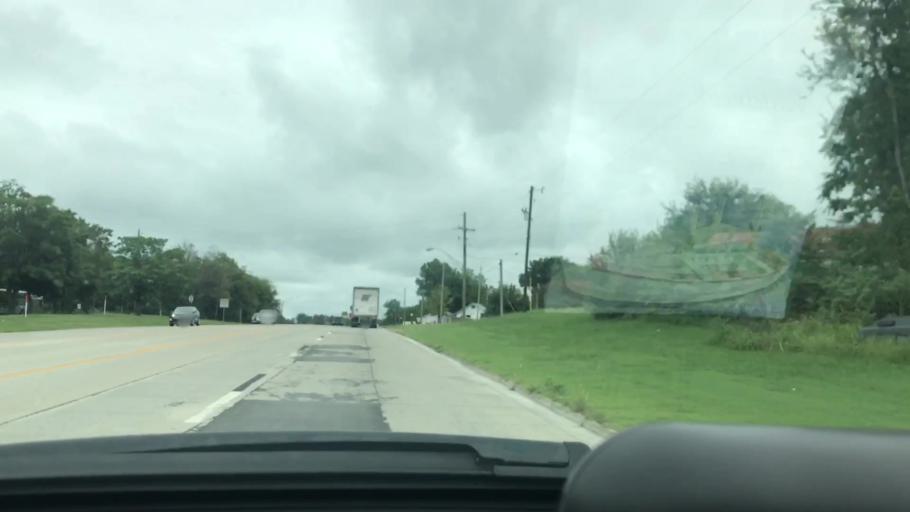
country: US
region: Oklahoma
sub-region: Pittsburg County
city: McAlester
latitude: 34.8241
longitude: -95.8479
